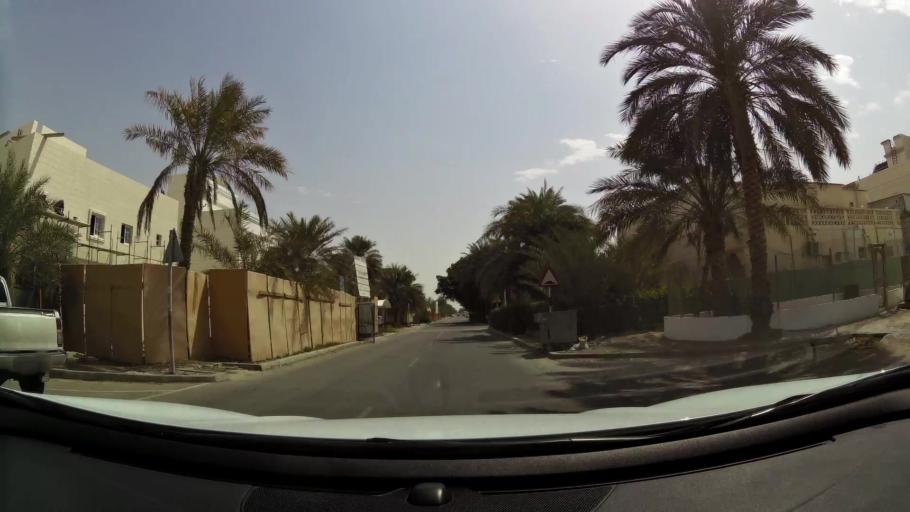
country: AE
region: Abu Dhabi
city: Abu Dhabi
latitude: 24.2957
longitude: 54.6321
